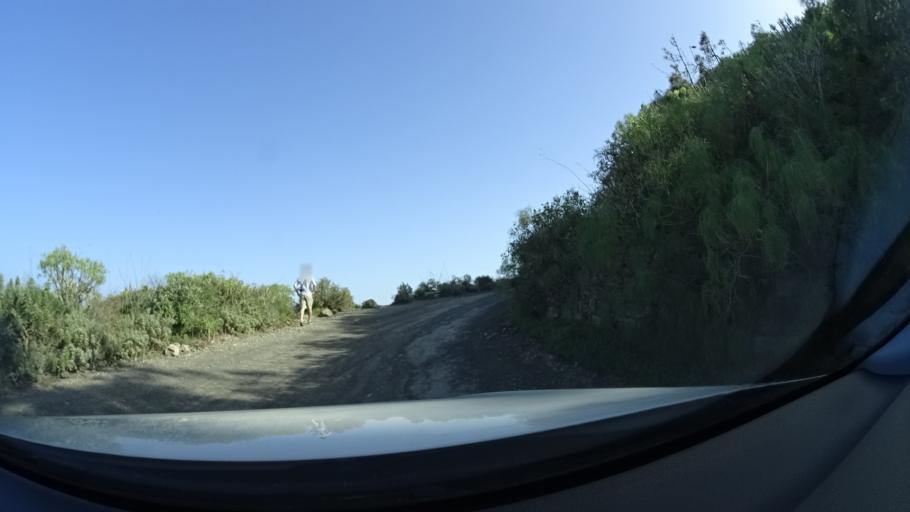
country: ES
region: Canary Islands
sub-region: Provincia de Las Palmas
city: Santa Brigida
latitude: 28.0325
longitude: -15.4598
